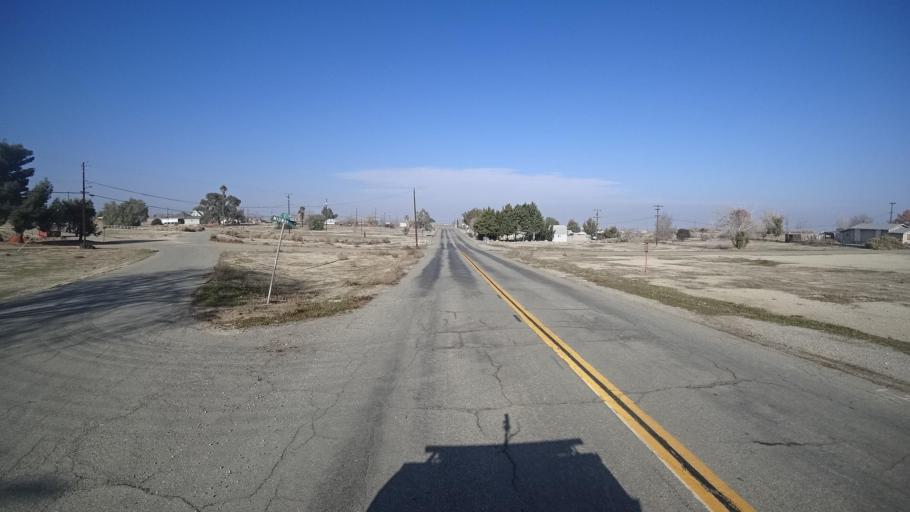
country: US
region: California
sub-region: Kern County
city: Taft Heights
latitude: 35.1767
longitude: -119.5402
